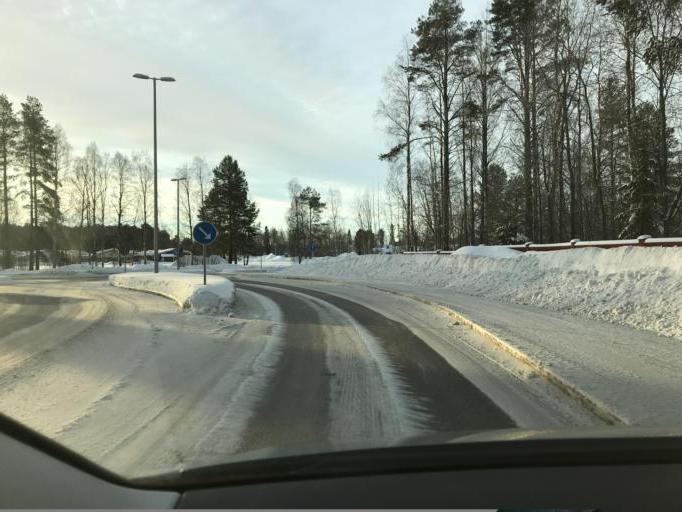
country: SE
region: Norrbotten
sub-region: Lulea Kommun
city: Bergnaset
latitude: 65.6144
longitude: 22.0981
